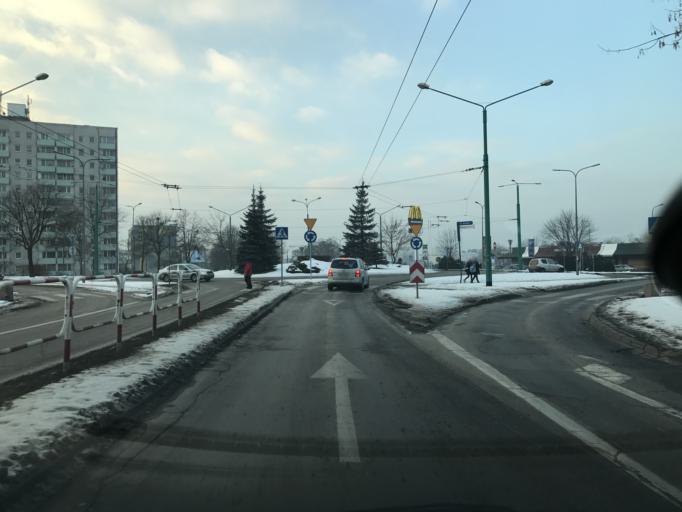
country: PL
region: Silesian Voivodeship
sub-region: Tychy
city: Tychy
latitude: 50.1102
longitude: 18.9792
